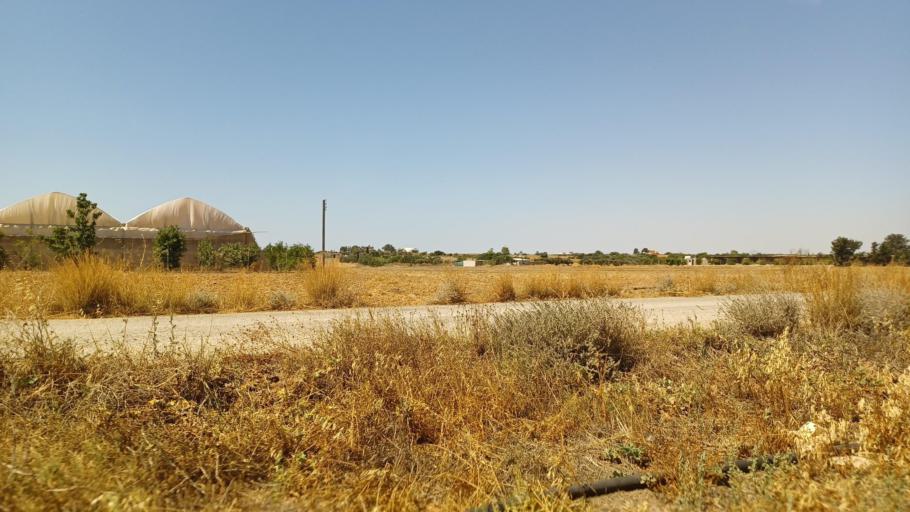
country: CY
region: Larnaka
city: Xylotymbou
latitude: 35.0247
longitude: 33.7291
